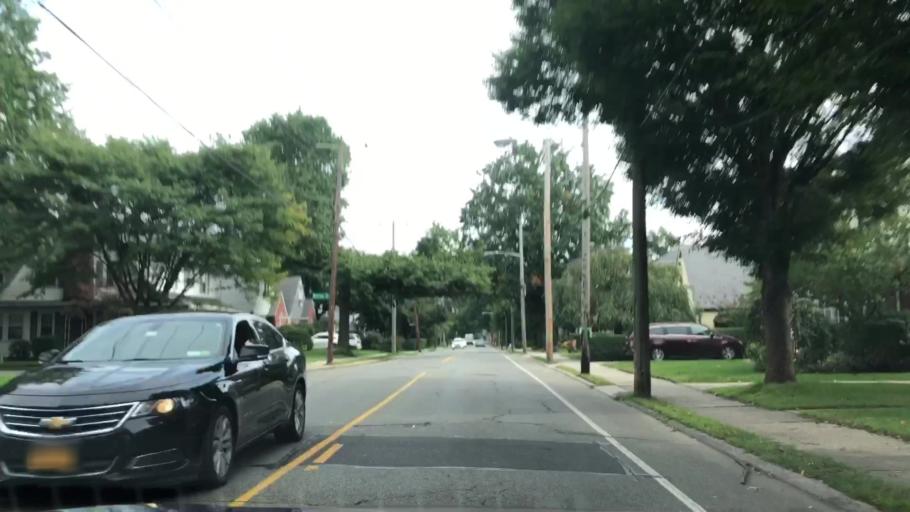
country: US
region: New York
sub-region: Nassau County
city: Floral Park
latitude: 40.7233
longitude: -73.7011
